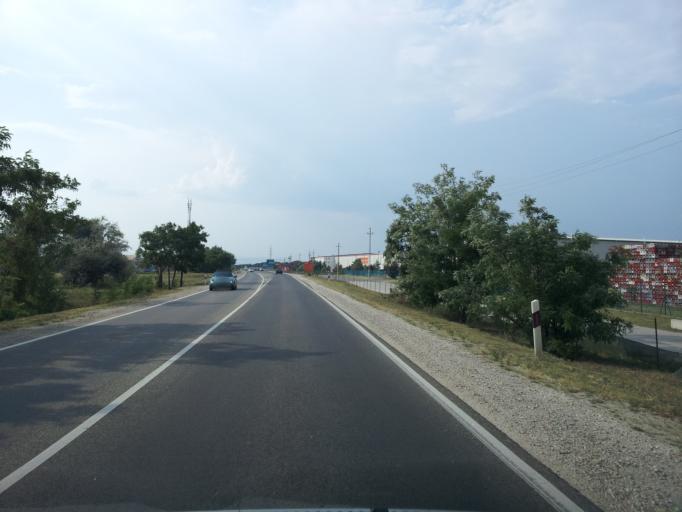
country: HU
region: Pest
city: Dunaharaszti
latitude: 47.3610
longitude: 19.1213
